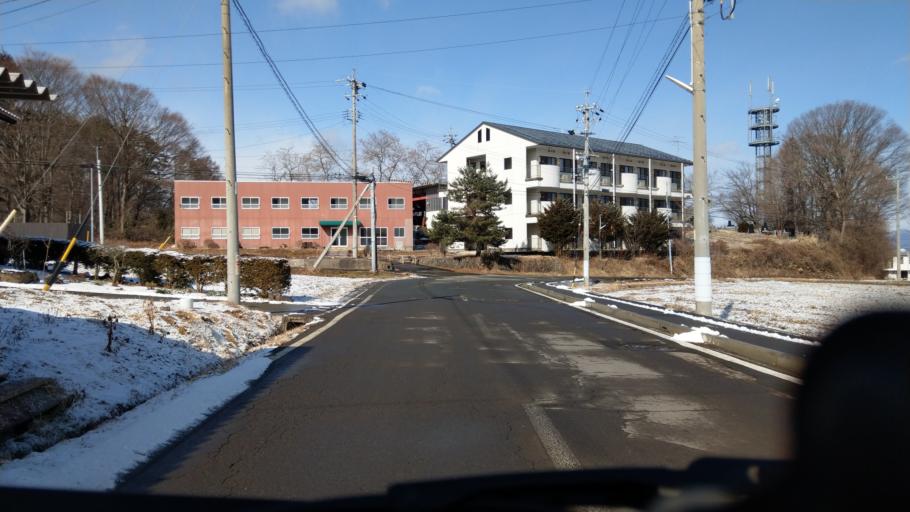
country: JP
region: Nagano
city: Kamimaruko
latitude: 36.2693
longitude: 138.3175
